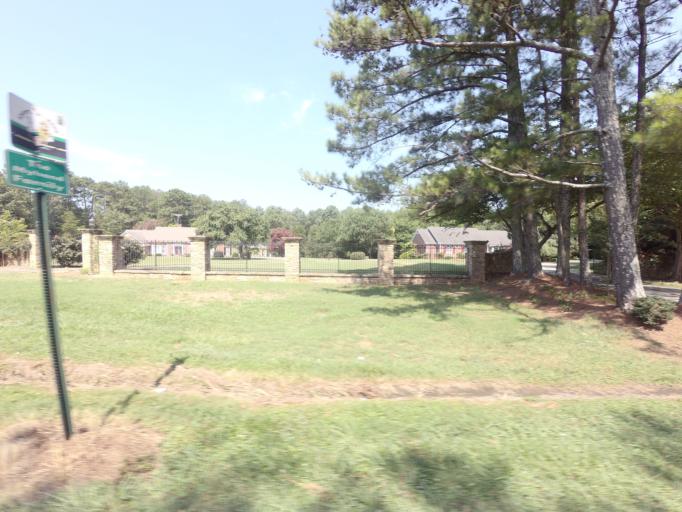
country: US
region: Georgia
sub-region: Fulton County
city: Alpharetta
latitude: 34.0152
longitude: -84.2807
